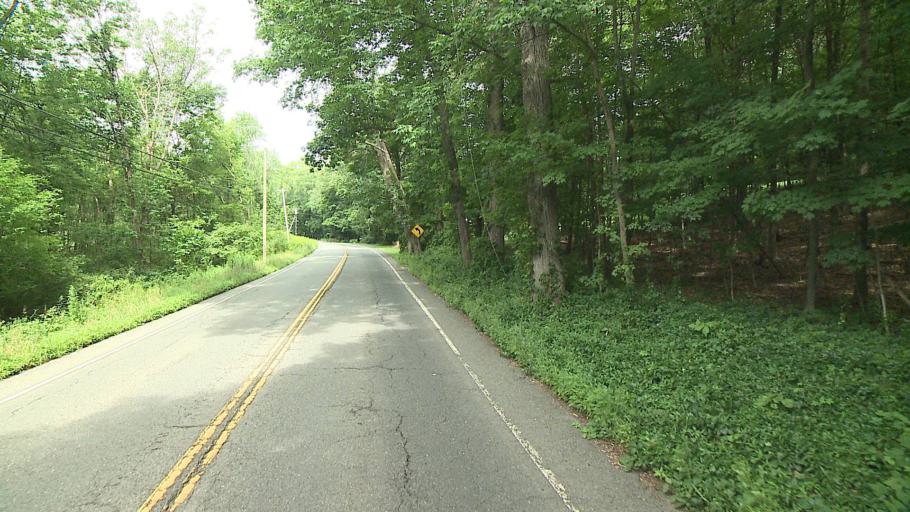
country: US
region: Connecticut
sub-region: Fairfield County
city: Sherman
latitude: 41.6477
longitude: -73.5061
